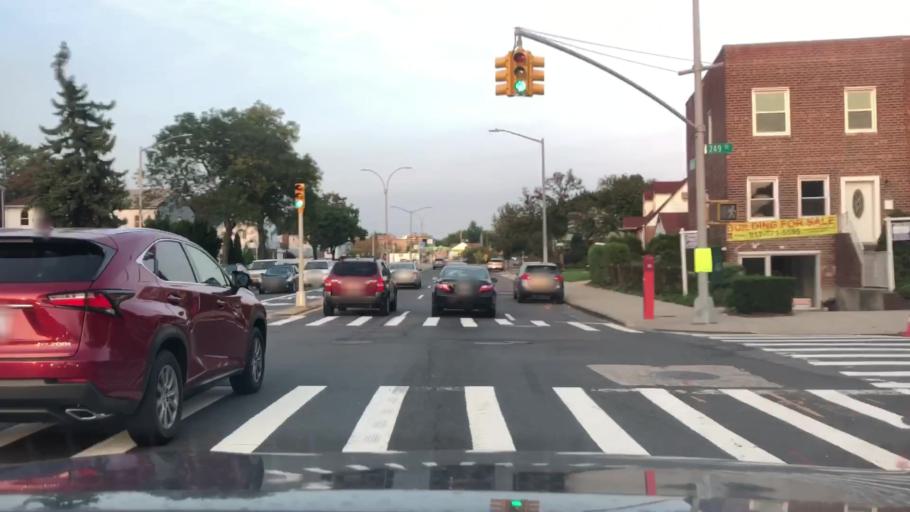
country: US
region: New York
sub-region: Nassau County
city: Bellerose
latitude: 40.7425
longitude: -73.7212
